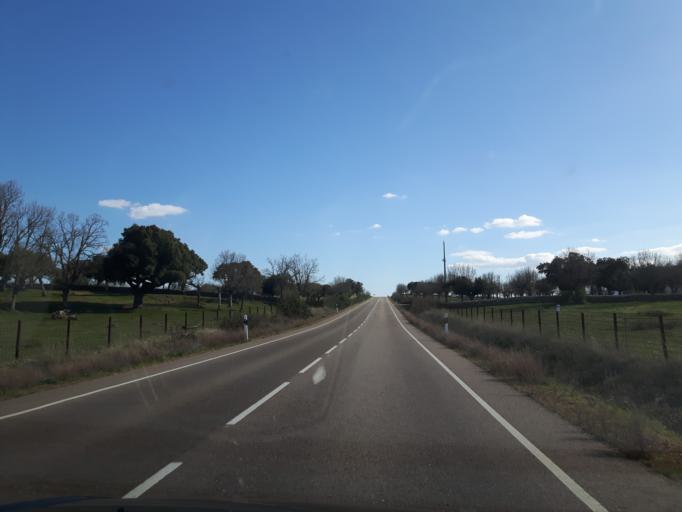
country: ES
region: Castille and Leon
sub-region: Provincia de Salamanca
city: Herguijuela del Campo
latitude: 40.6530
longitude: -5.9002
